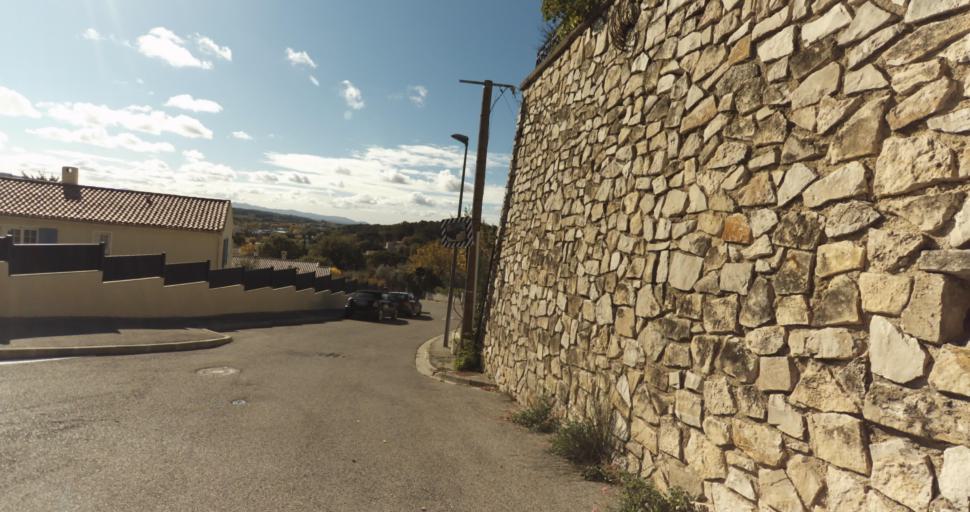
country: FR
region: Provence-Alpes-Cote d'Azur
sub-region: Departement des Bouches-du-Rhone
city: Venelles
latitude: 43.5978
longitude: 5.4771
